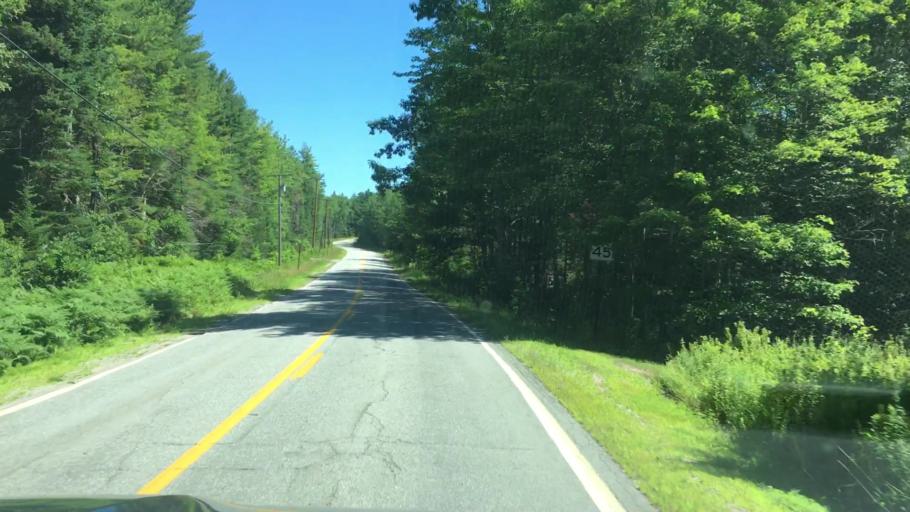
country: US
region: Maine
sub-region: Hancock County
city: Penobscot
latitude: 44.4702
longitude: -68.7040
